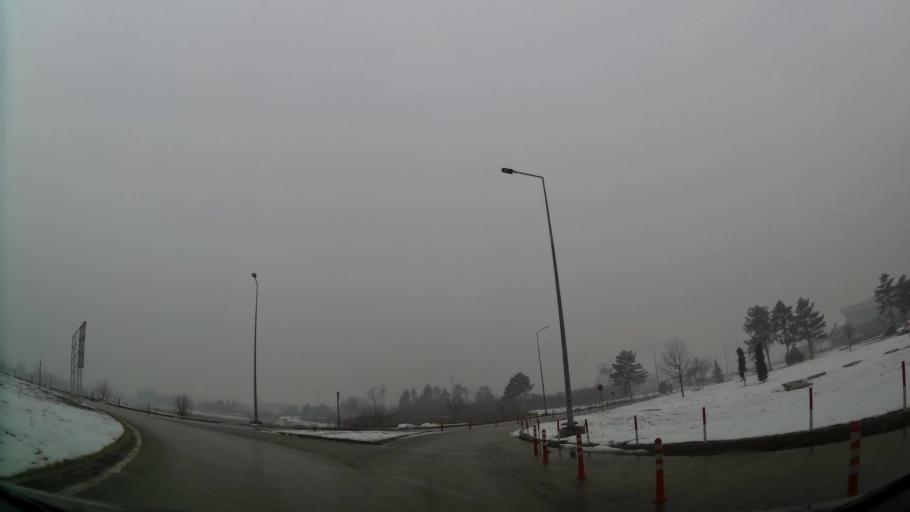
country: MK
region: Petrovec
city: Petrovec
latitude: 41.9599
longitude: 21.6296
